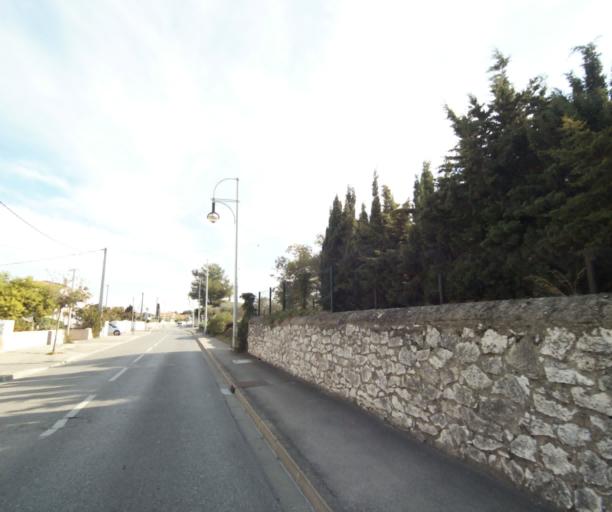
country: FR
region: Provence-Alpes-Cote d'Azur
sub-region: Departement des Bouches-du-Rhone
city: Chateauneuf-les-Martigues
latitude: 43.3960
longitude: 5.1189
